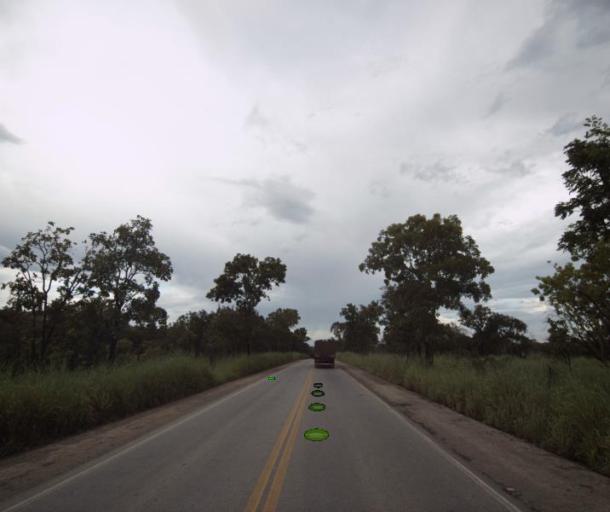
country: BR
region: Goias
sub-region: Porangatu
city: Porangatu
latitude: -13.6168
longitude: -49.0424
